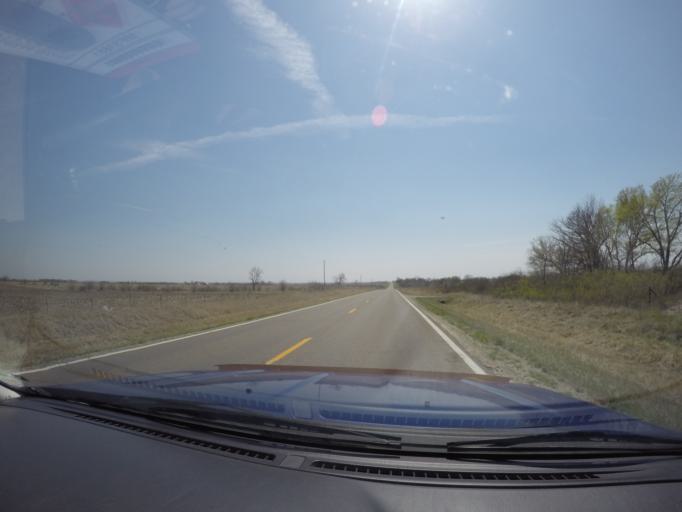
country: US
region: Kansas
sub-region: Morris County
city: Council Grove
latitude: 38.7907
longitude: -96.5013
